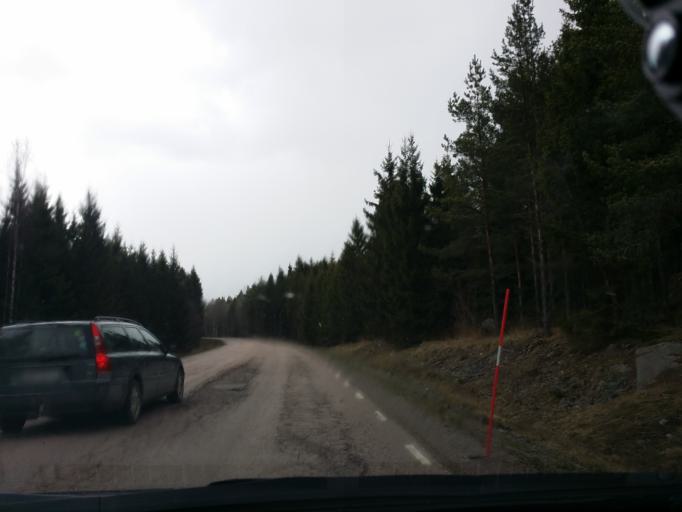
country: SE
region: Uppsala
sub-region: Enkopings Kommun
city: Enkoping
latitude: 59.6317
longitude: 17.1442
